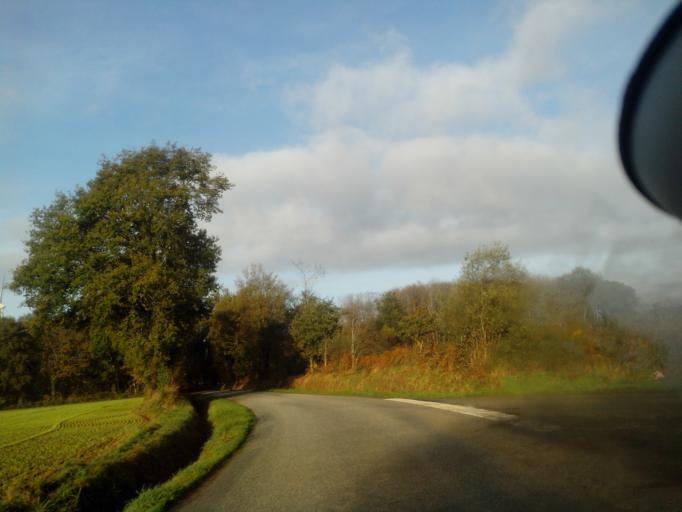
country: FR
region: Brittany
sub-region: Departement du Morbihan
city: Meneac
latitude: 48.1249
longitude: -2.4370
